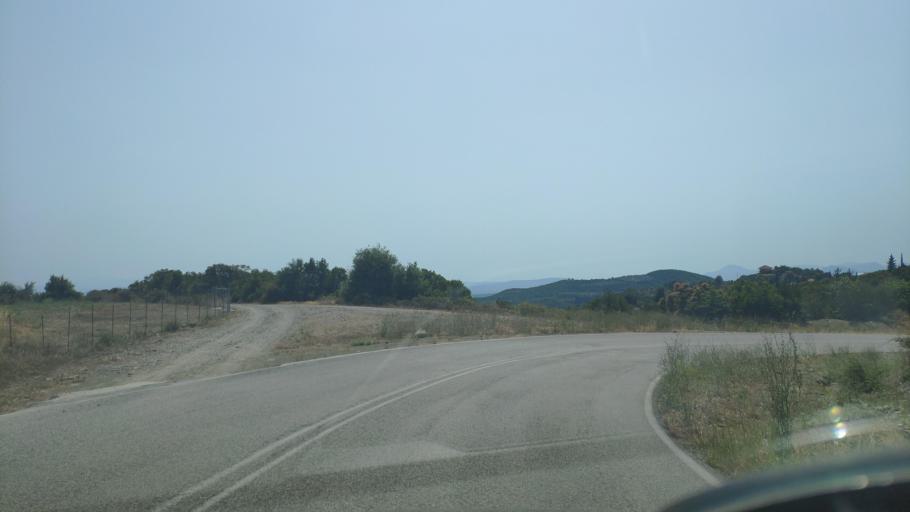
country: GR
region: Epirus
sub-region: Nomos Artas
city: Peta
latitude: 39.1786
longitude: 21.0893
